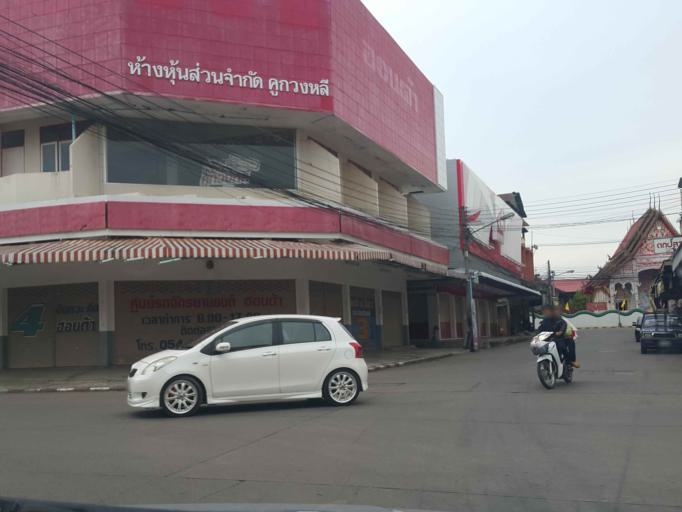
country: TH
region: Nan
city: Nan
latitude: 18.7794
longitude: 100.7774
